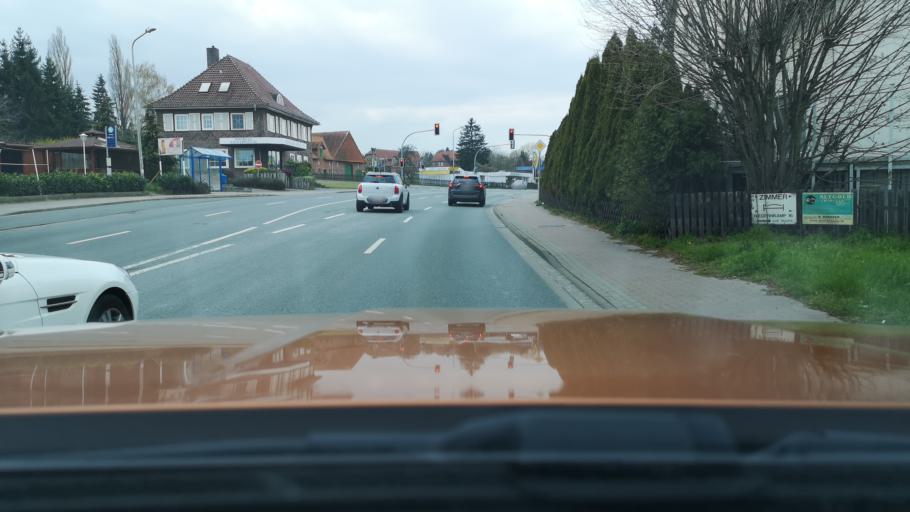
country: DE
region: Lower Saxony
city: Nienstadt
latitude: 52.2937
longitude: 9.1687
